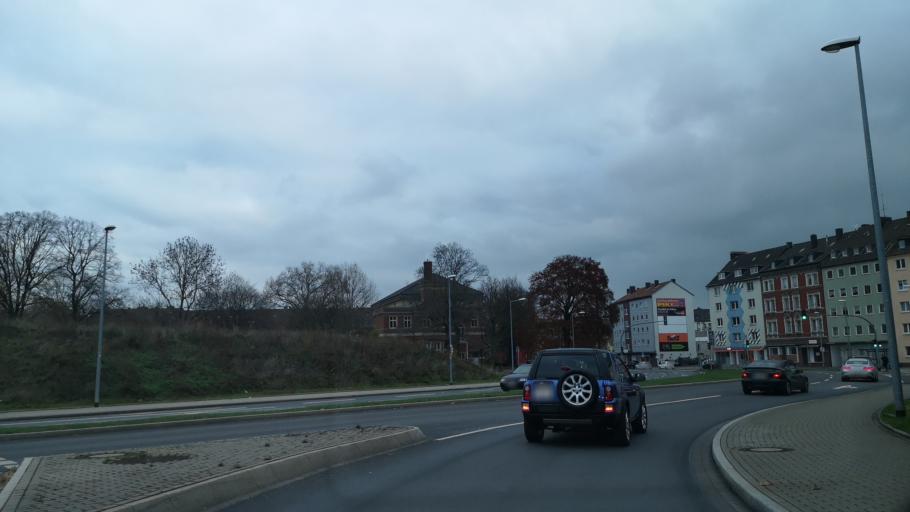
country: DE
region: North Rhine-Westphalia
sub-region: Regierungsbezirk Arnsberg
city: Hagen
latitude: 51.3566
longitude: 7.4543
